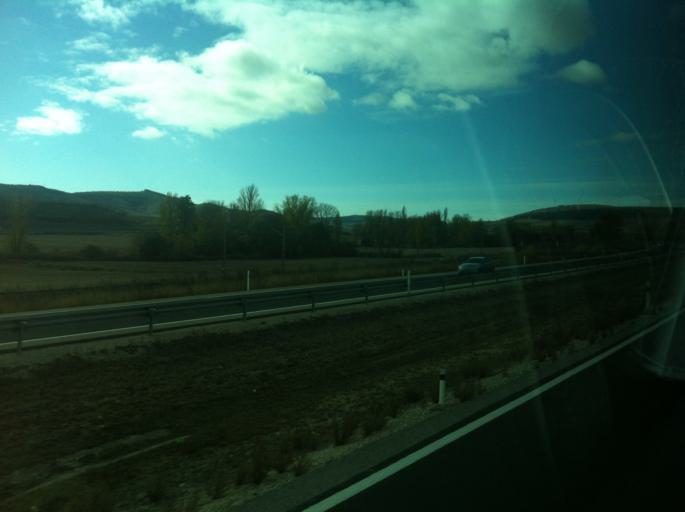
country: ES
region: Castille and Leon
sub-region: Provincia de Burgos
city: Quintanavides
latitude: 42.4834
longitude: -3.4118
